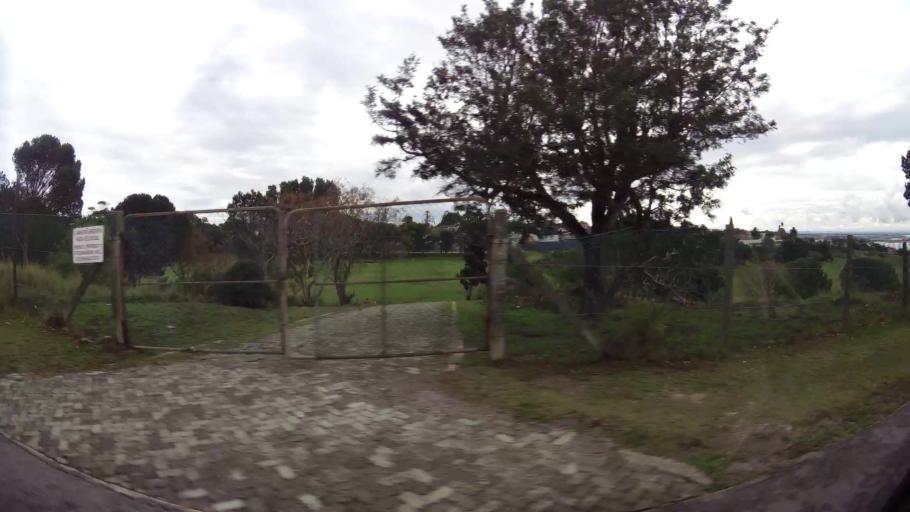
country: ZA
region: Eastern Cape
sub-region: Nelson Mandela Bay Metropolitan Municipality
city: Port Elizabeth
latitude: -33.9504
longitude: 25.5939
